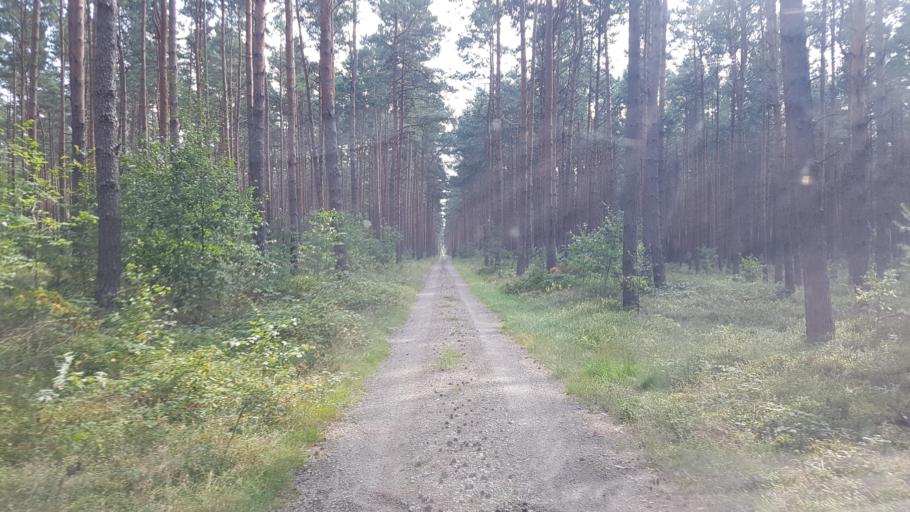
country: DE
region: Brandenburg
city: Hohenbucko
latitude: 51.7682
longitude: 13.5402
